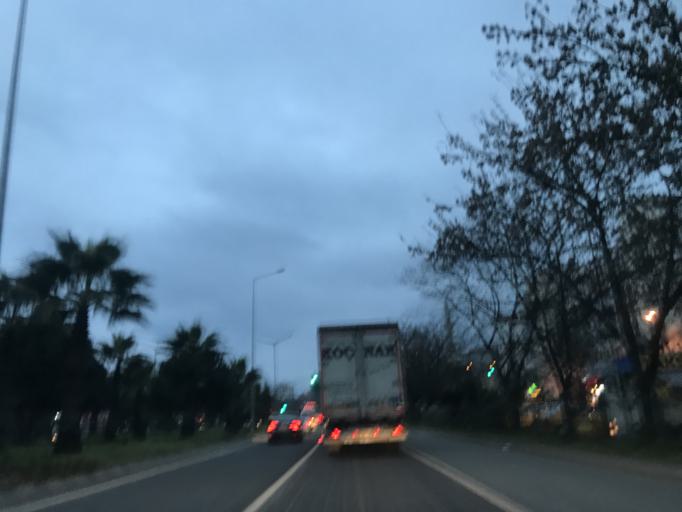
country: TR
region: Trabzon
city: Akcaabat
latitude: 41.0226
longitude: 39.5698
